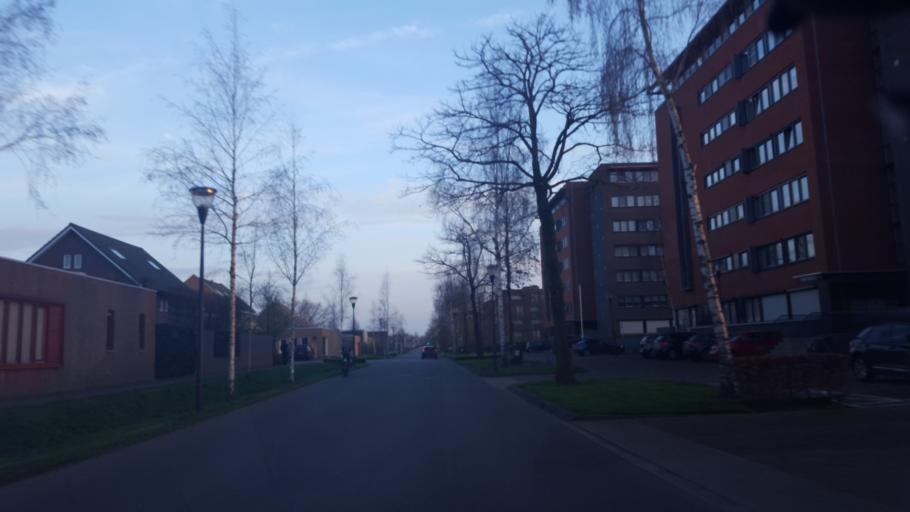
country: NL
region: North Brabant
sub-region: Gemeente Eindhoven
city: Meerhoven
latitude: 51.4388
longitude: 5.4099
